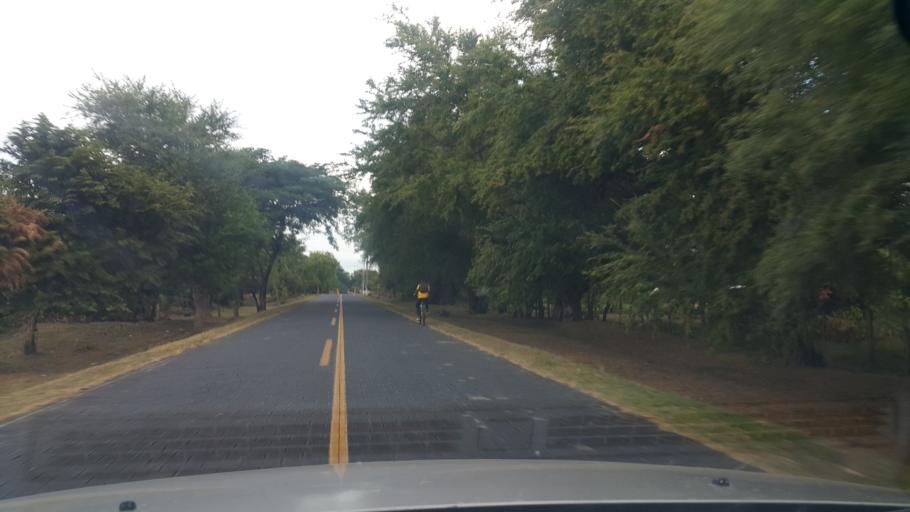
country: NI
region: Rivas
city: Moyogalpa
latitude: 11.5205
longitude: -85.7043
